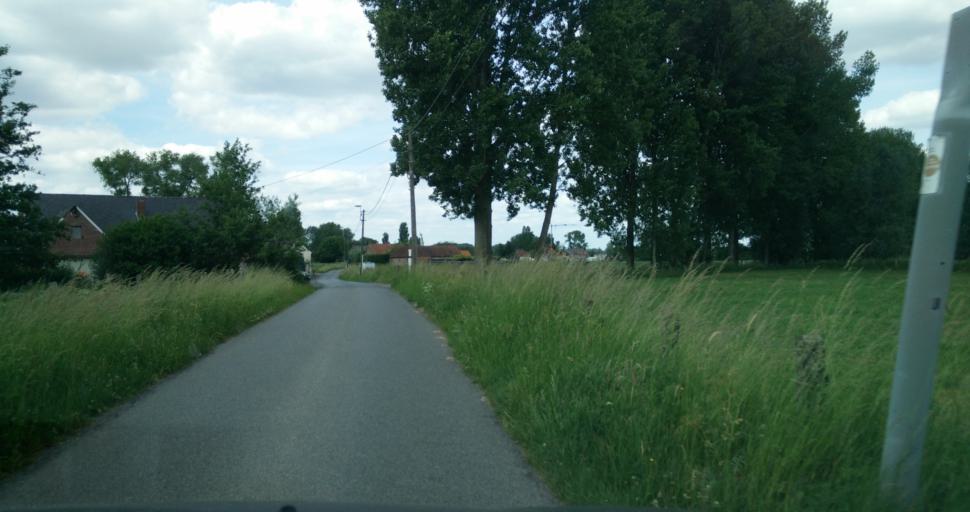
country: BE
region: Wallonia
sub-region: Province du Hainaut
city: Flobecq
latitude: 50.7931
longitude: 3.7412
